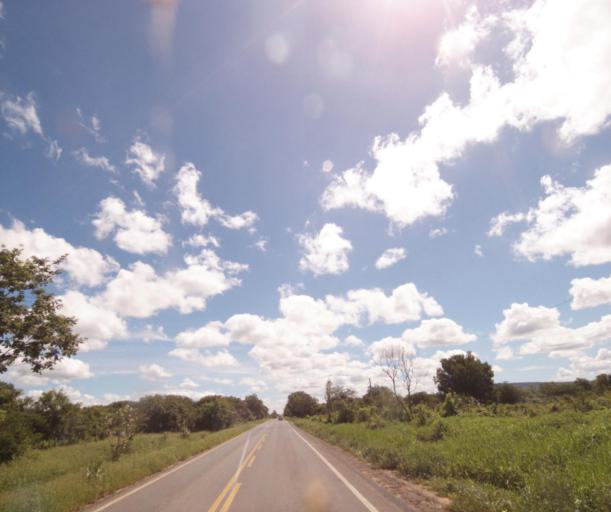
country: BR
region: Bahia
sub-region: Sao Felix Do Coribe
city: Santa Maria da Vitoria
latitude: -13.4055
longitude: -44.1553
